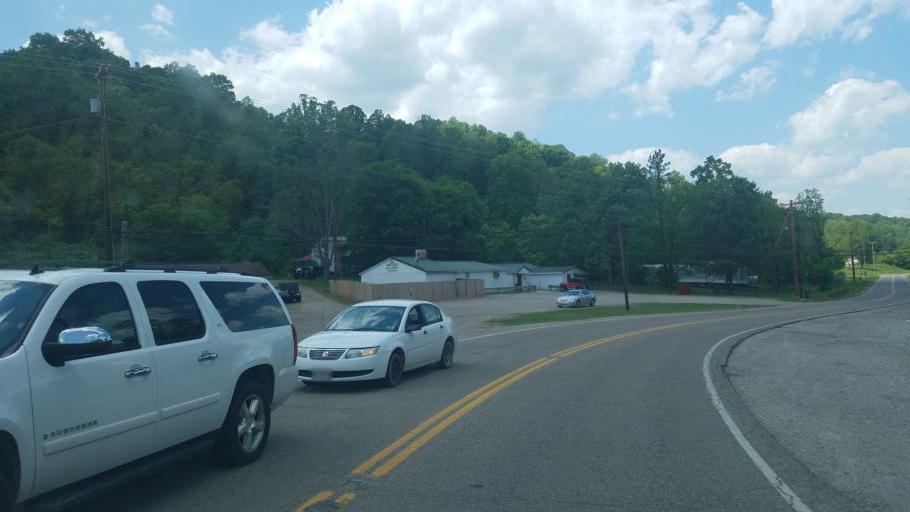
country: US
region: Ohio
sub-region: Meigs County
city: Pomeroy
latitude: 39.0388
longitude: -82.0615
